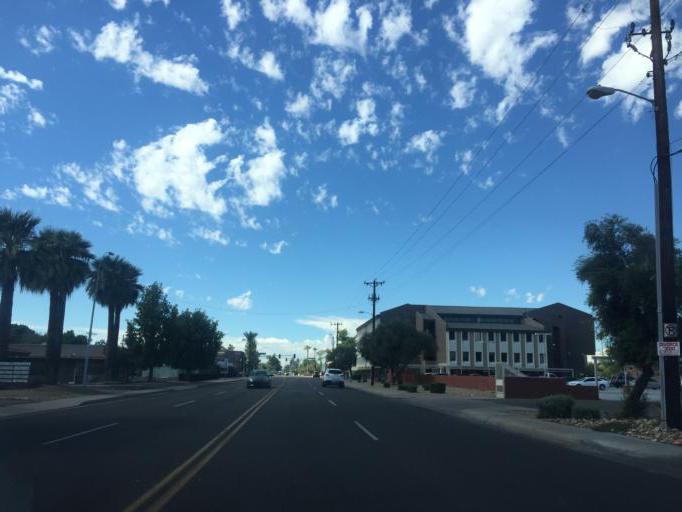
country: US
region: Arizona
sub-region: Maricopa County
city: Phoenix
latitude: 33.5169
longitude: -112.0975
